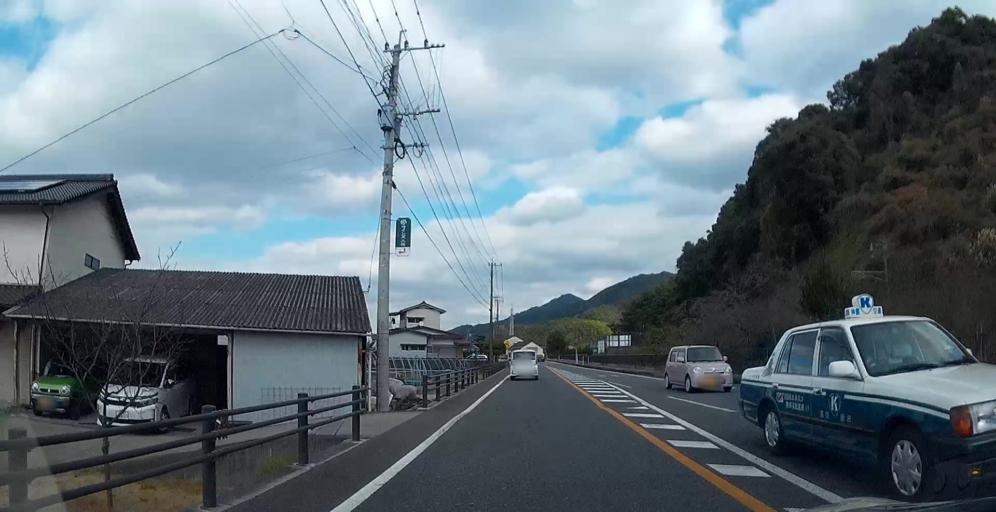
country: JP
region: Kumamoto
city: Yatsushiro
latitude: 32.4493
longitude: 130.5903
